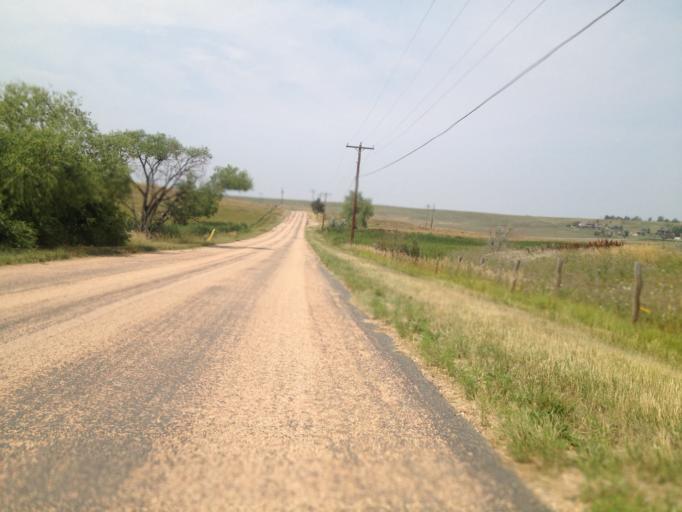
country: US
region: Colorado
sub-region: Boulder County
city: Superior
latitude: 39.9547
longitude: -105.1988
